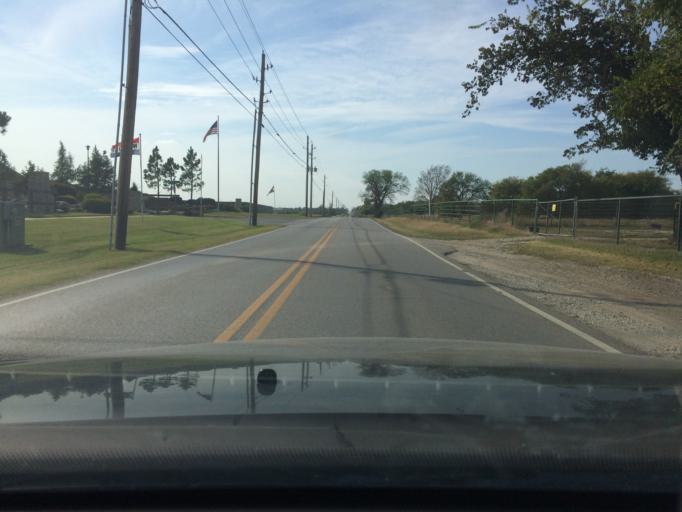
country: US
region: Oklahoma
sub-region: Tulsa County
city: Broken Arrow
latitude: 36.1045
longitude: -95.7643
